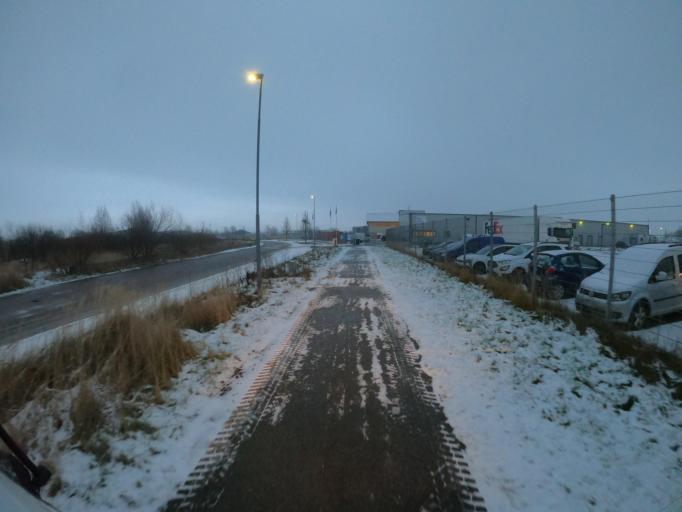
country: SE
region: Skane
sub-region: Svedala Kommun
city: Svedala
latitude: 55.5123
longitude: 13.2563
